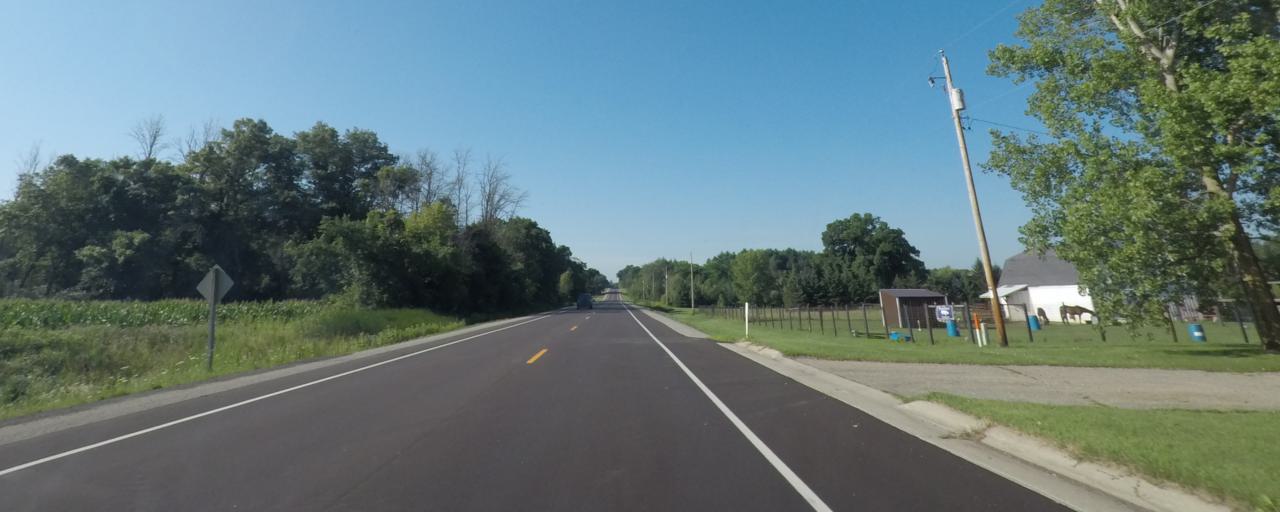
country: US
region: Wisconsin
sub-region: Jefferson County
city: Palmyra
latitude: 42.9336
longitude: -88.5864
